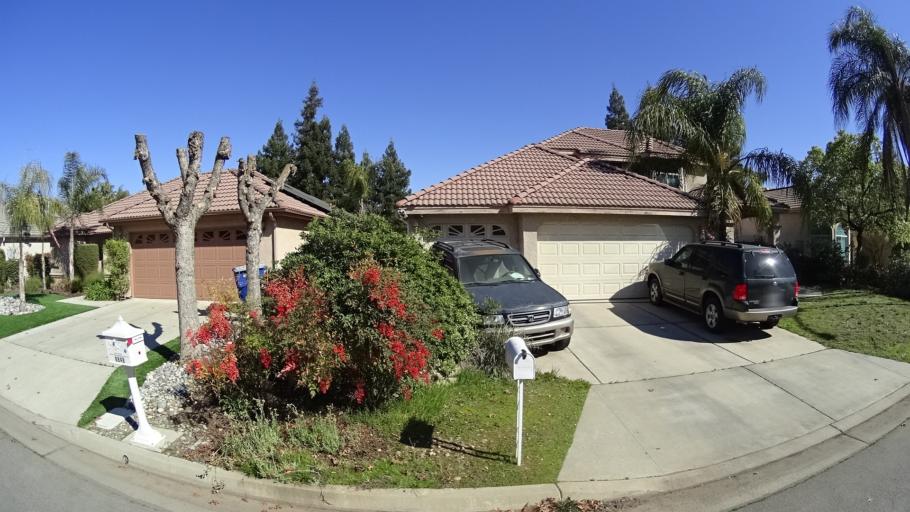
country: US
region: California
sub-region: Fresno County
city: Clovis
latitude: 36.8646
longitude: -119.7450
